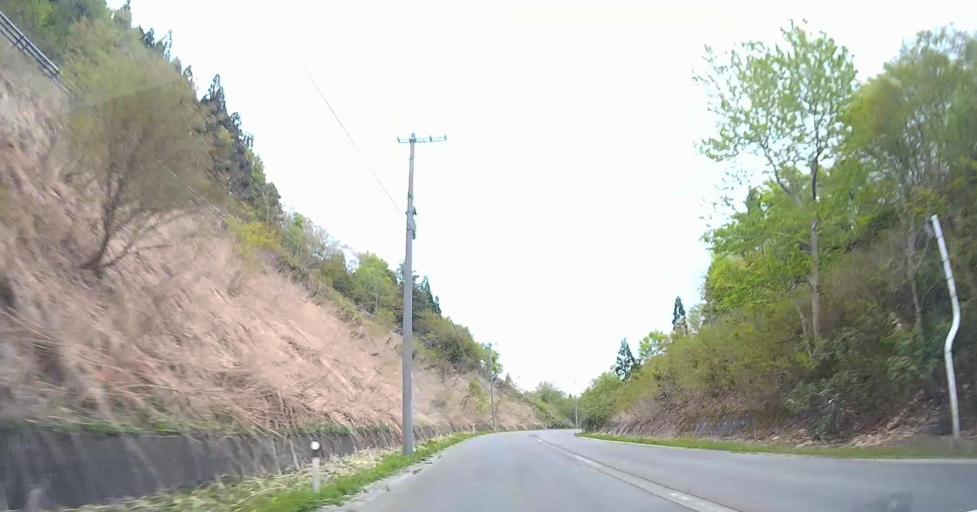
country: JP
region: Aomori
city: Goshogawara
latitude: 41.1084
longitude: 140.5366
